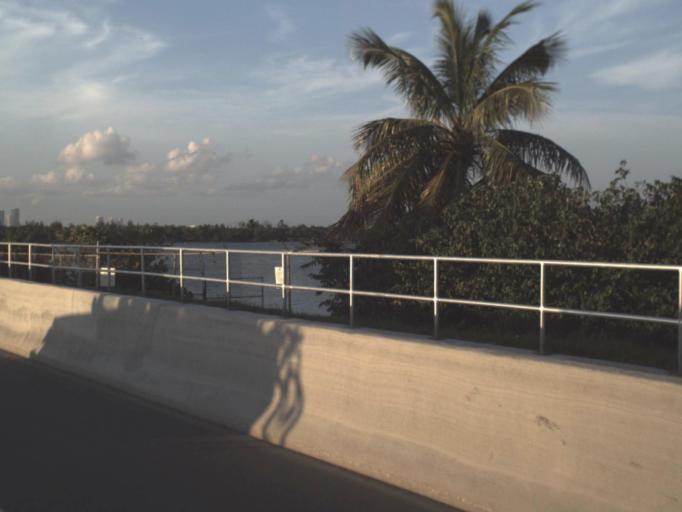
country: US
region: Florida
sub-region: Miami-Dade County
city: Key Biscayne
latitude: 25.7282
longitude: -80.1561
